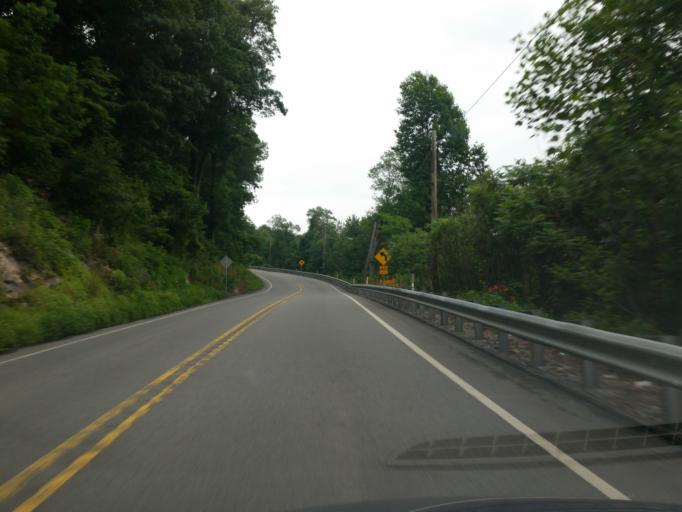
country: US
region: Pennsylvania
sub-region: Schuylkill County
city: Valley View
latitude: 40.6104
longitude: -76.4724
